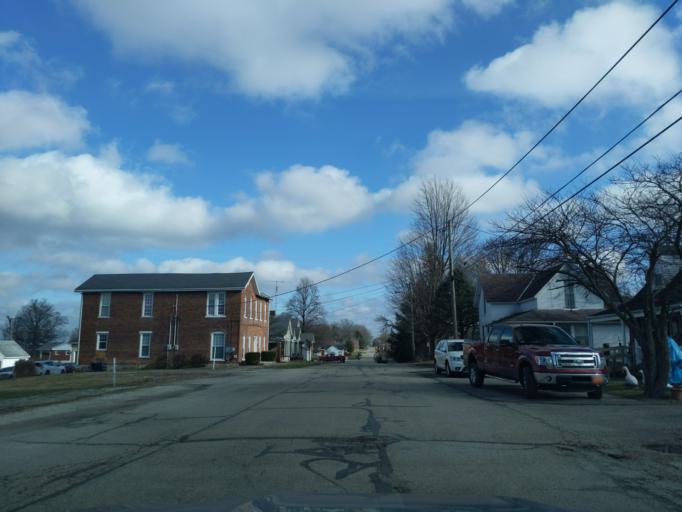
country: US
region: Indiana
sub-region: Ripley County
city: Batesville
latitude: 39.3093
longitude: -85.3308
